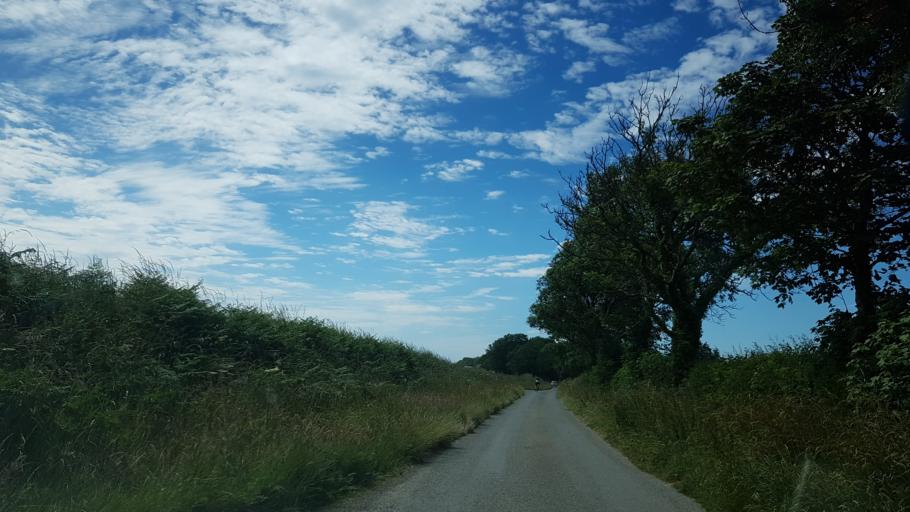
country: GB
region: Wales
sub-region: Pembrokeshire
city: Wiston
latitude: 51.8279
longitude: -4.8921
